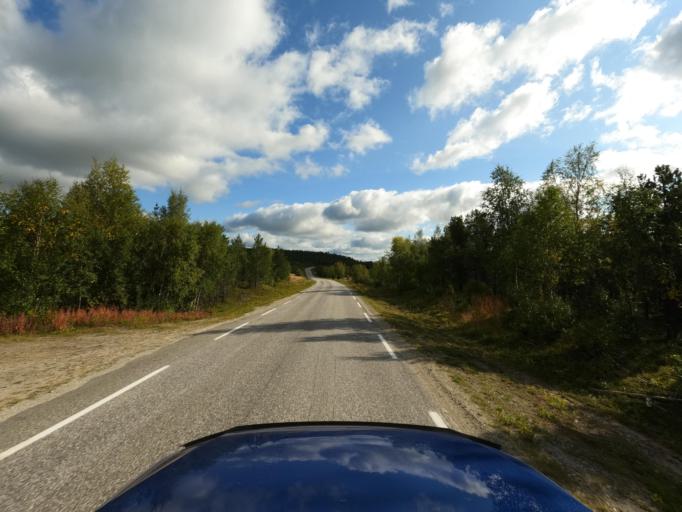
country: NO
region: Finnmark Fylke
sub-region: Karasjok
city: Karasjohka
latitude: 69.4436
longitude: 25.2332
